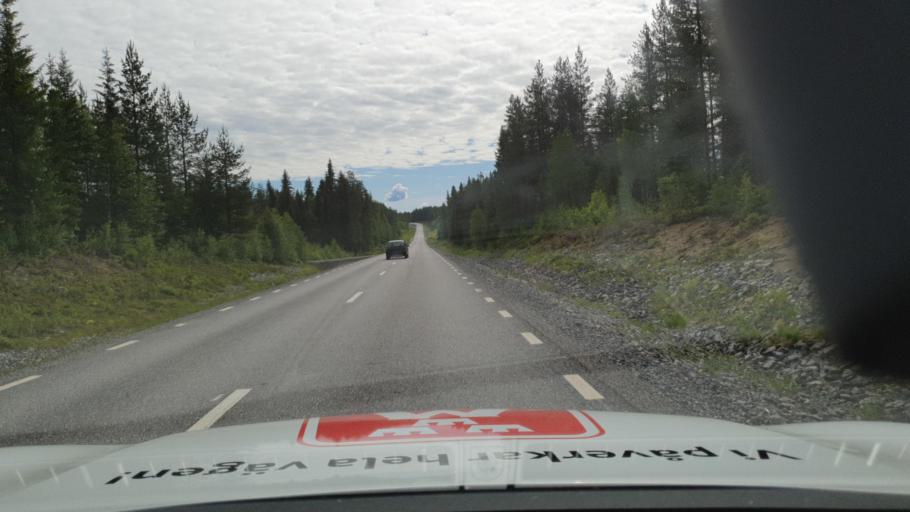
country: SE
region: Vaesterbotten
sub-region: Vindelns Kommun
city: Vindeln
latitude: 64.2505
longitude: 19.9944
